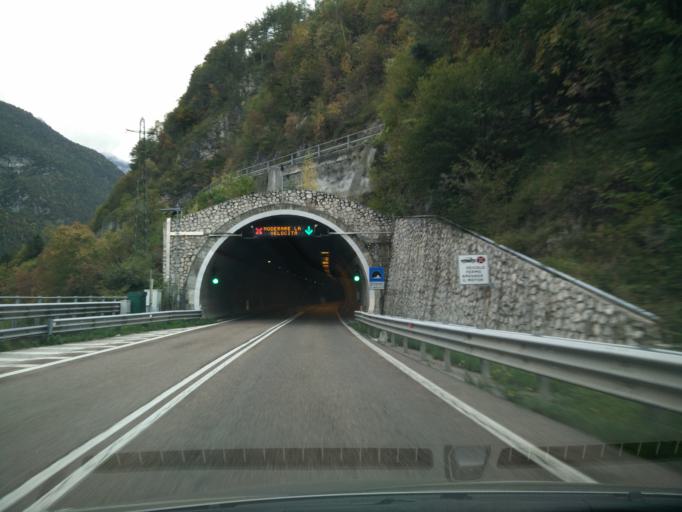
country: IT
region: Veneto
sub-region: Provincia di Belluno
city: Ospitale di Cadore
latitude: 46.3421
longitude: 12.3304
